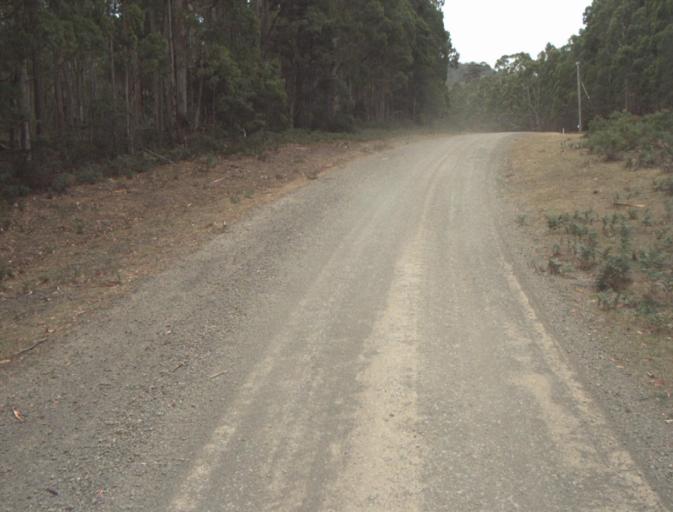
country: AU
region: Tasmania
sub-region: Dorset
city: Scottsdale
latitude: -41.4358
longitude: 147.5149
